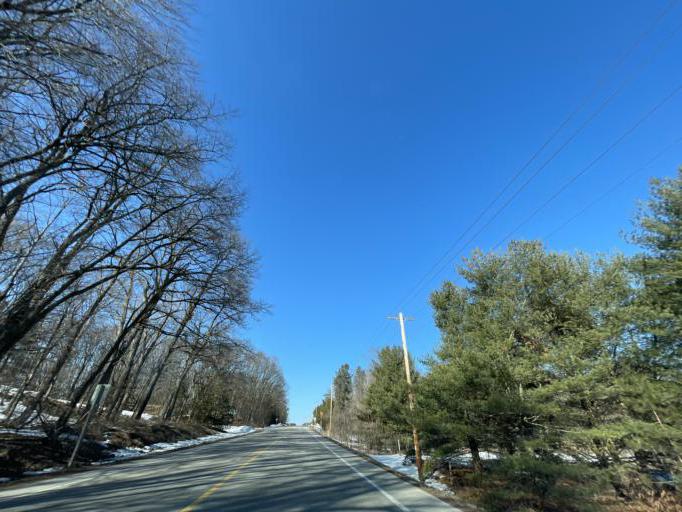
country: US
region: Wisconsin
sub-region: Brown County
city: Suamico
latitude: 44.6547
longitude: -88.0903
